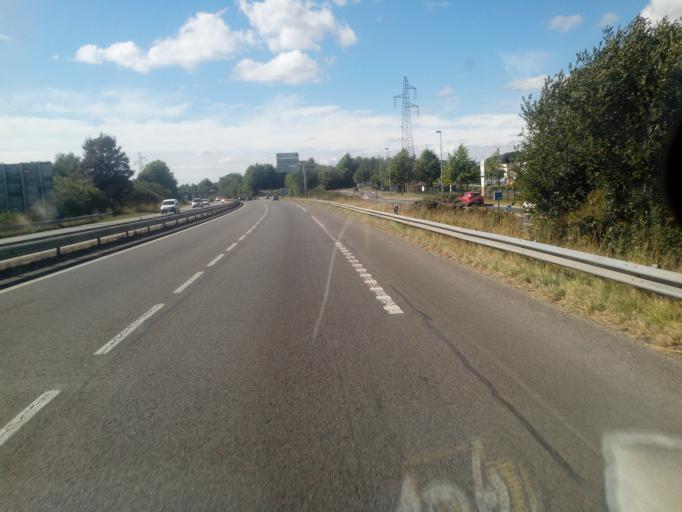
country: FR
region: Pays de la Loire
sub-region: Departement de la Loire-Atlantique
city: Orvault
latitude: 47.2743
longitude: -1.5940
